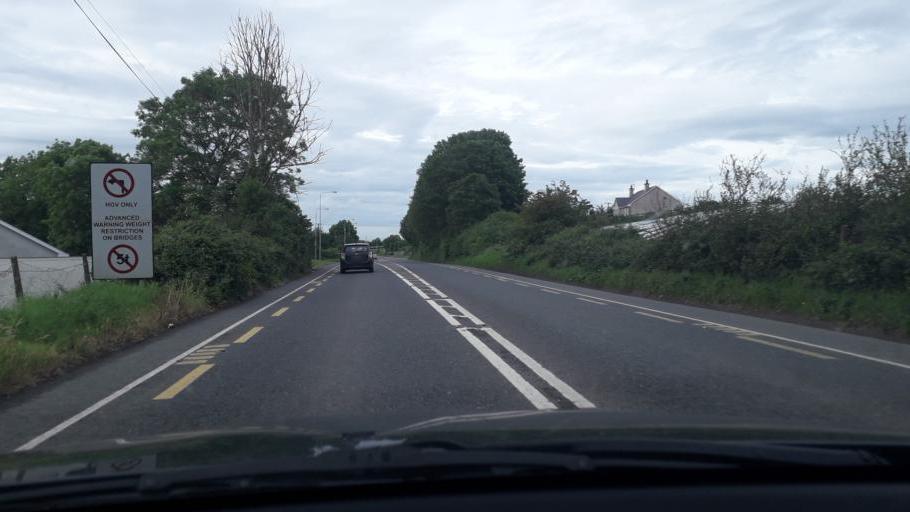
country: IE
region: Leinster
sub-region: County Carlow
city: Carlow
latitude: 52.7816
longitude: -6.9509
